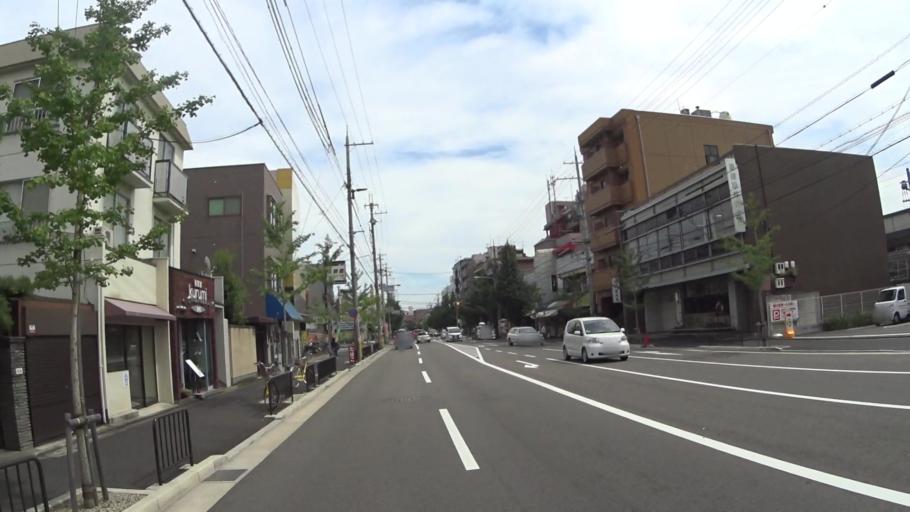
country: JP
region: Kyoto
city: Kyoto
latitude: 35.0192
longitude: 135.7258
